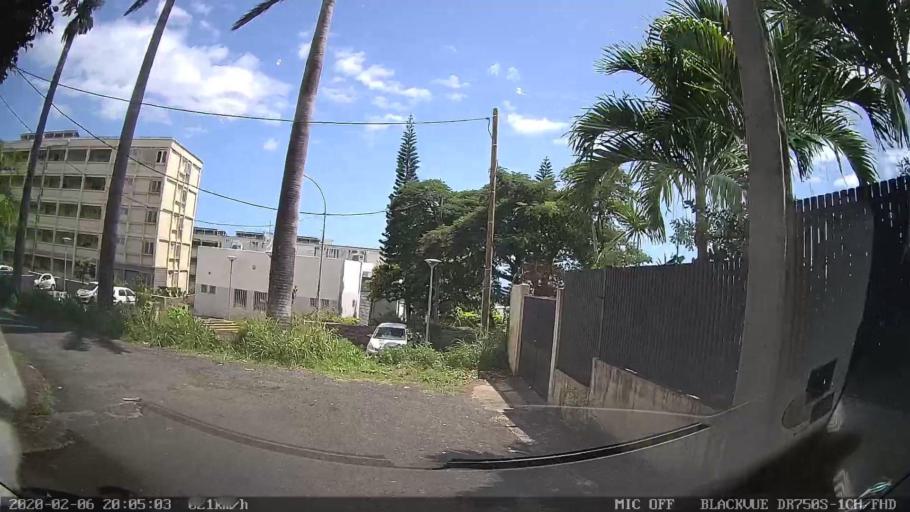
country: RE
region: Reunion
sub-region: Reunion
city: Saint-Denis
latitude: -20.8963
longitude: 55.4627
